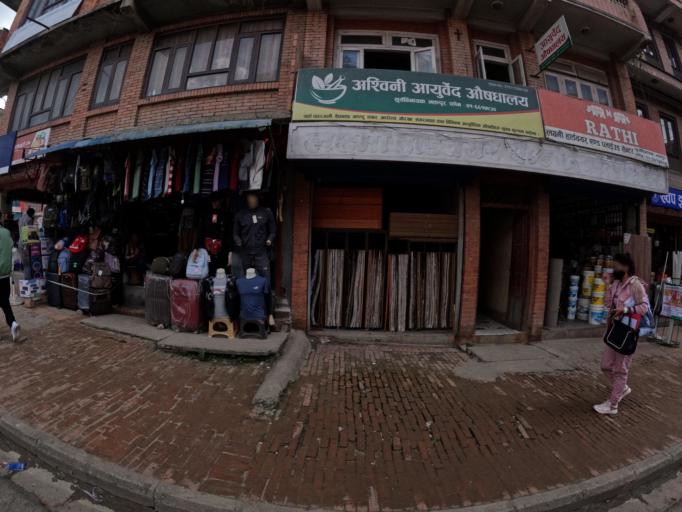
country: NP
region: Central Region
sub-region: Bagmati Zone
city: Bhaktapur
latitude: 27.6660
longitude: 85.4256
